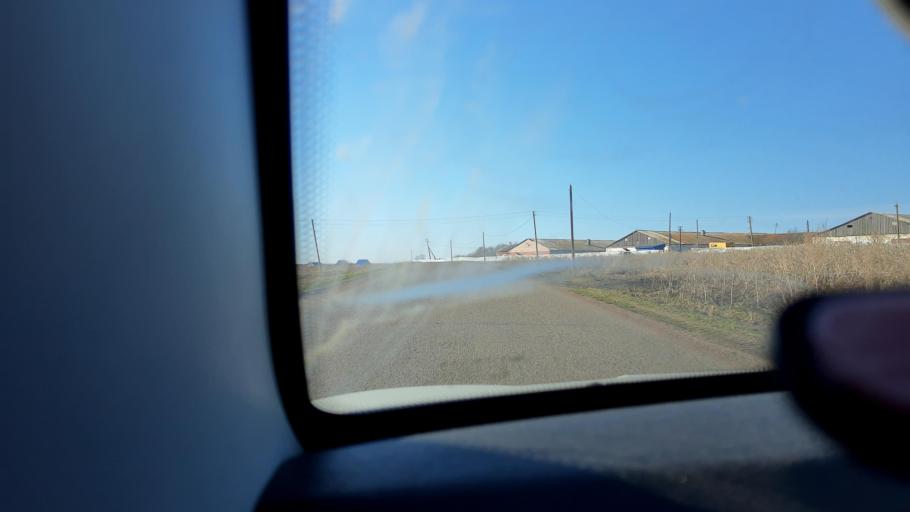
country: RU
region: Bashkortostan
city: Asanovo
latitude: 54.7877
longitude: 55.5042
